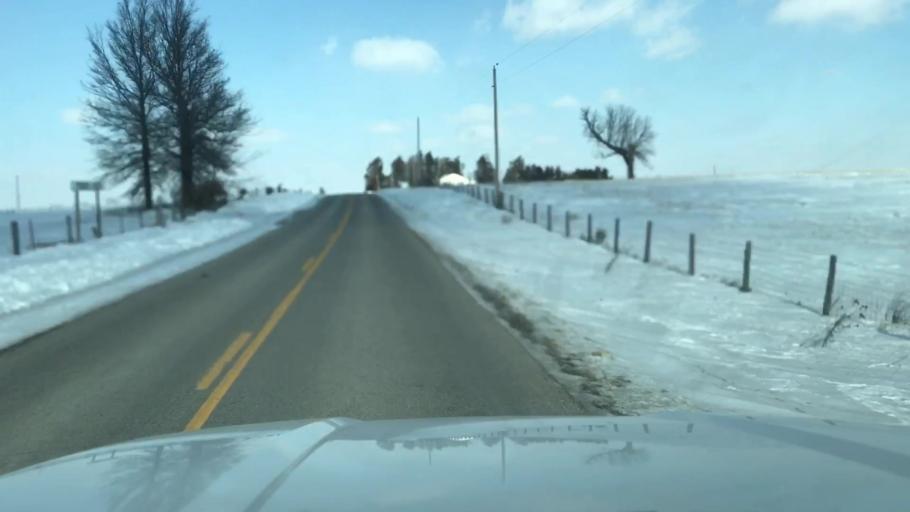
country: US
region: Missouri
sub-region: Nodaway County
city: Maryville
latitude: 40.3713
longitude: -94.7215
